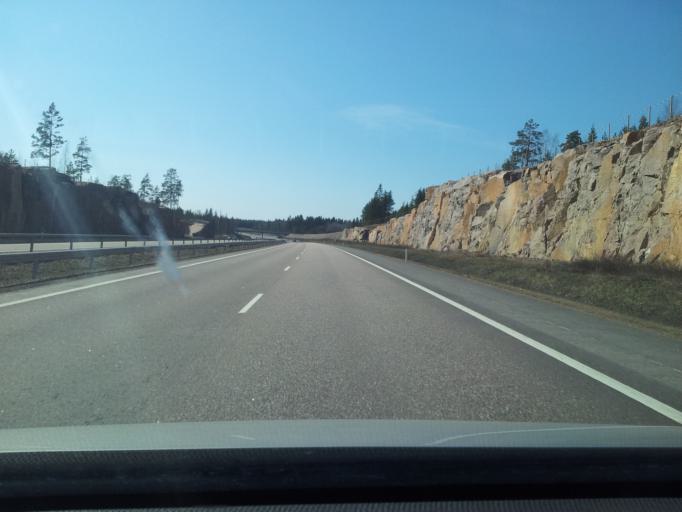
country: FI
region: Uusimaa
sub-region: Loviisa
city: Lovisa
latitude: 60.4900
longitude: 26.3242
